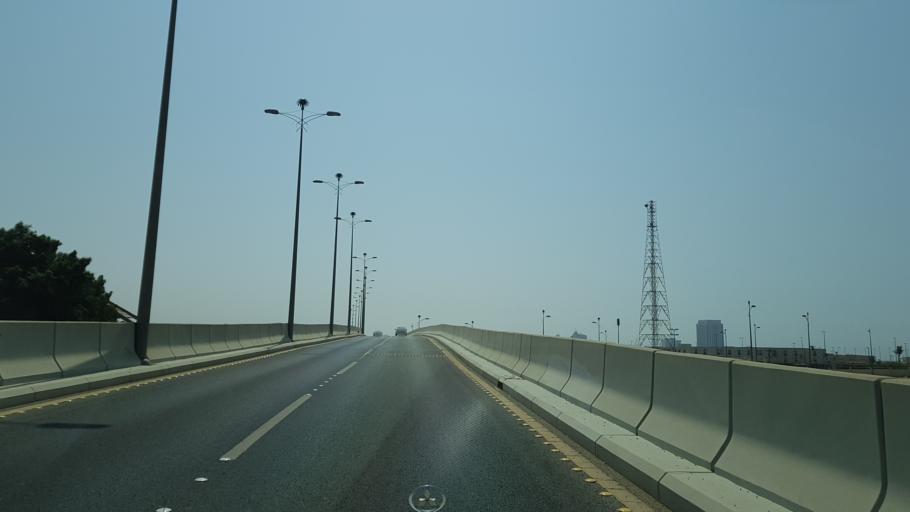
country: SA
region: Makkah
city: Jeddah
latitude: 21.5429
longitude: 39.1549
